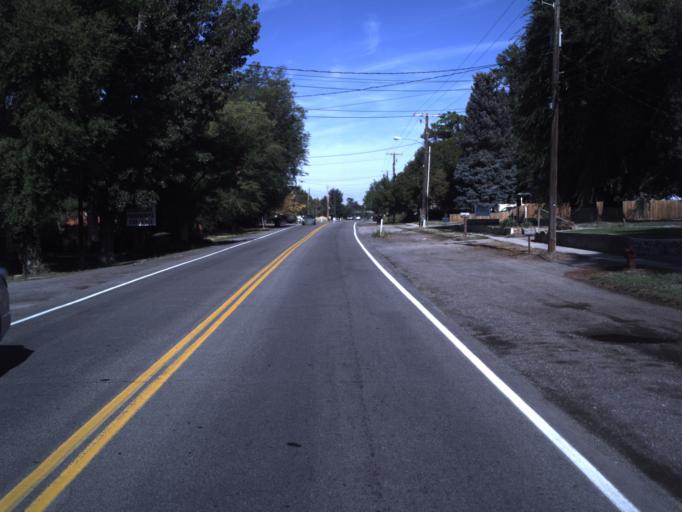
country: US
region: Utah
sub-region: Utah County
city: Provo
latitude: 40.2468
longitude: -111.6997
